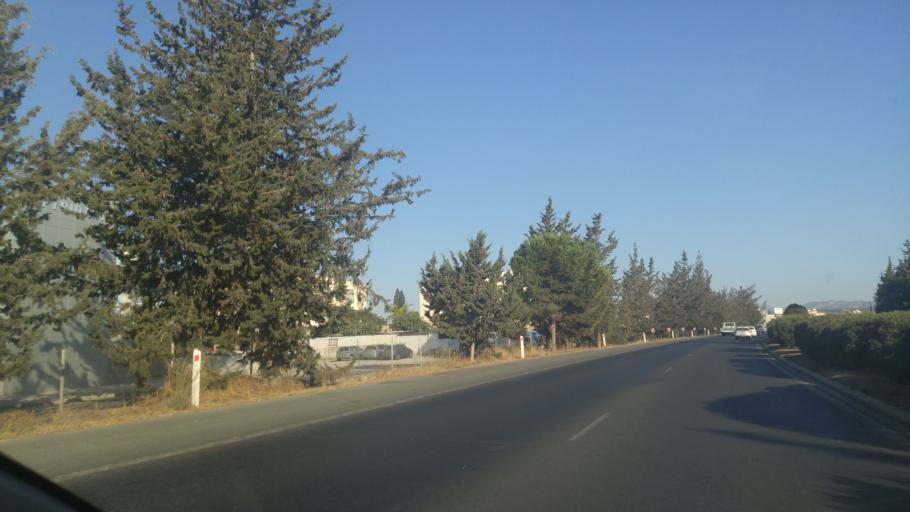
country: CY
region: Limassol
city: Pano Polemidia
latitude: 34.6821
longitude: 33.0085
